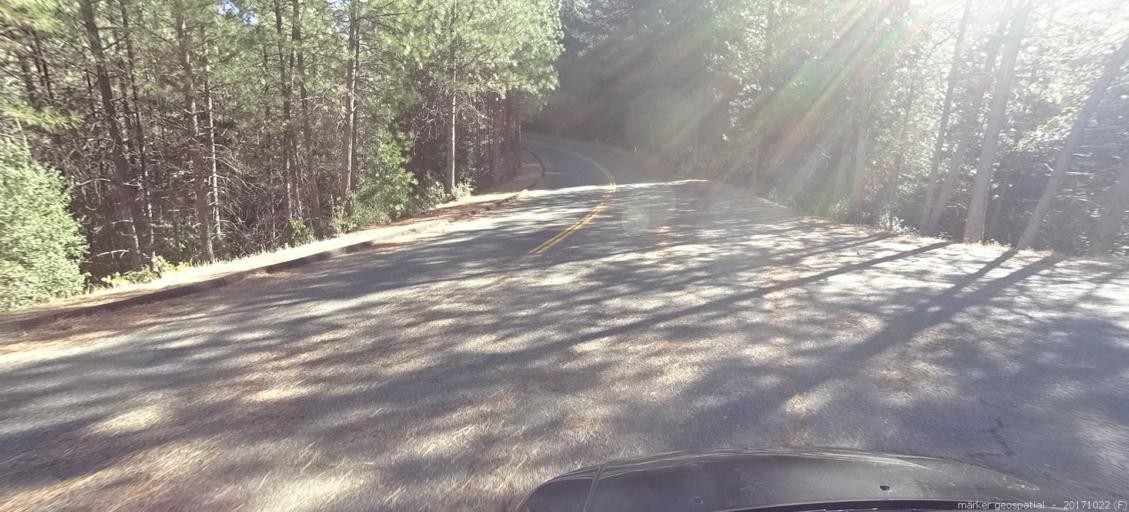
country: US
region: California
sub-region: Shasta County
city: Central Valley (historical)
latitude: 40.9217
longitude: -122.4107
